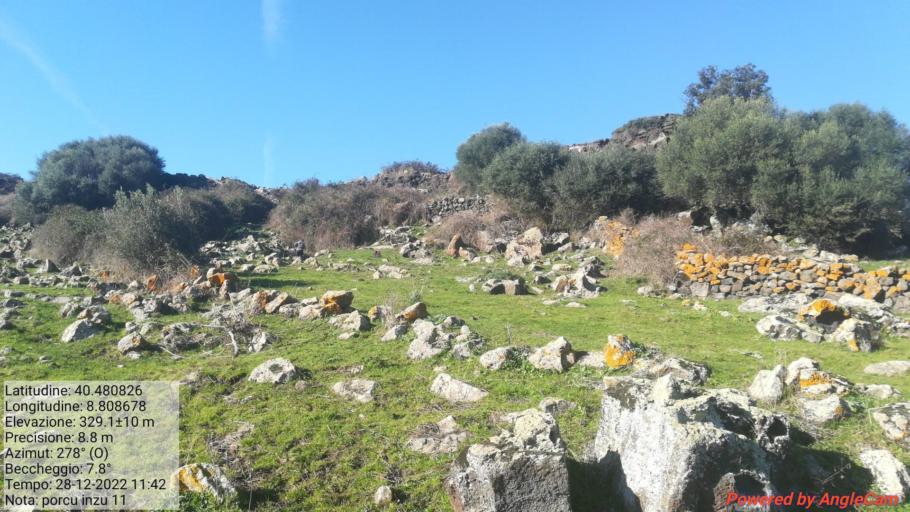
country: IT
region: Sardinia
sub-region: Provincia di Sassari
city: Torralba
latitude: 40.4808
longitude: 8.8087
